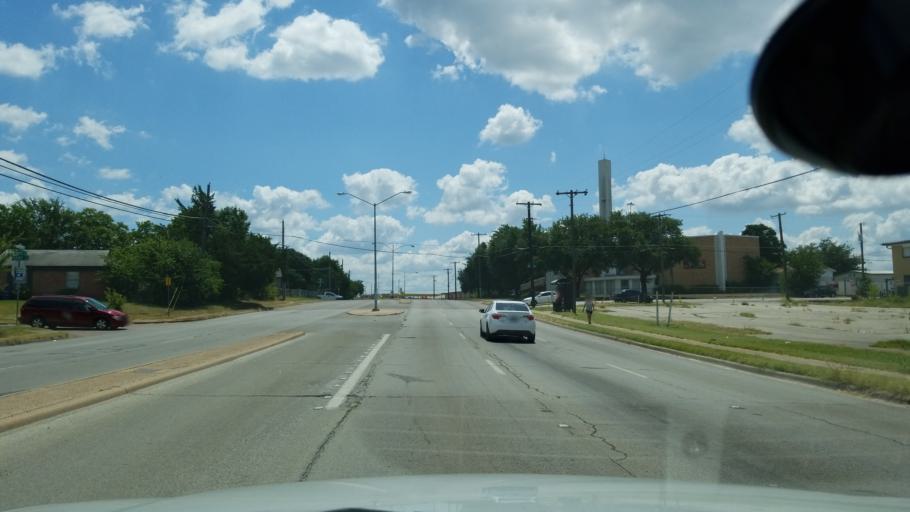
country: US
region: Texas
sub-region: Dallas County
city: Cockrell Hill
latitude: 32.7056
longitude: -96.8367
